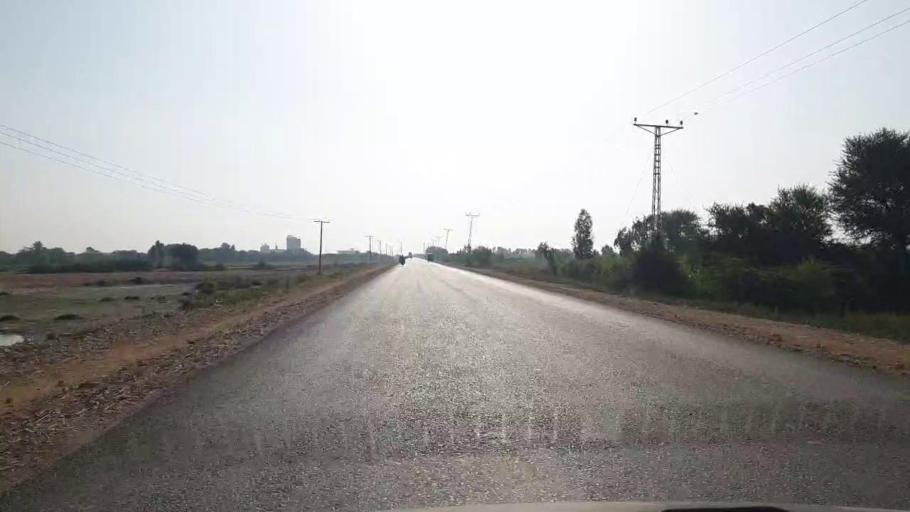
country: PK
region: Sindh
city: Badin
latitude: 24.6638
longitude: 68.8732
